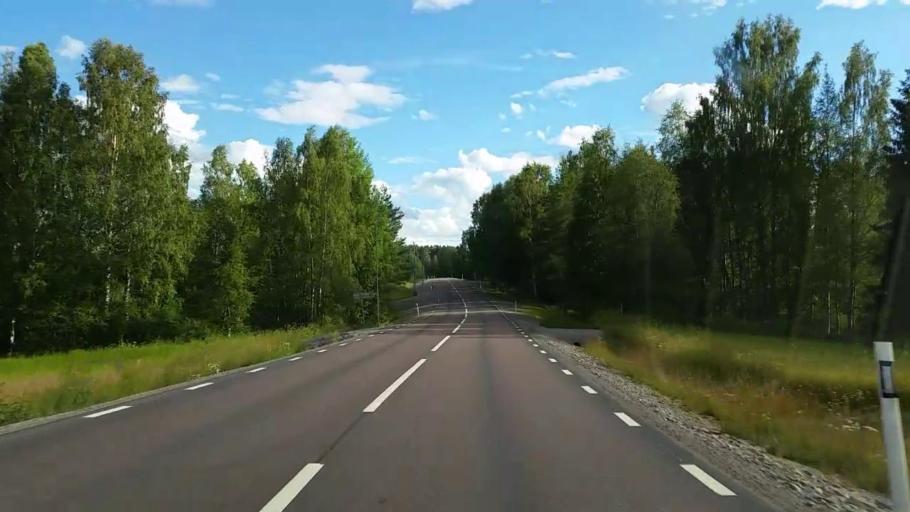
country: SE
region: Gaevleborg
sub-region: Ljusdals Kommun
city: Ljusdal
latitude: 61.8432
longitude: 16.0025
